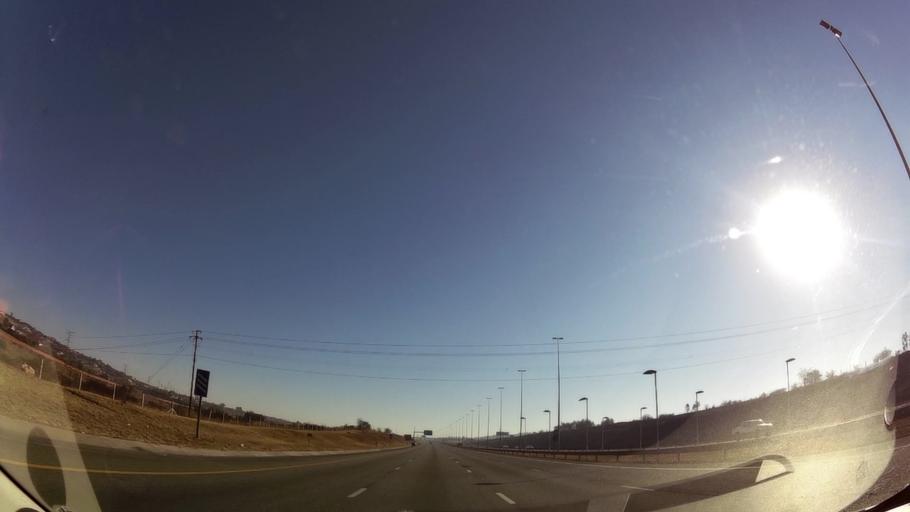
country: ZA
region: Gauteng
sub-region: City of Tshwane Metropolitan Municipality
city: Centurion
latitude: -25.8763
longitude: 28.2545
